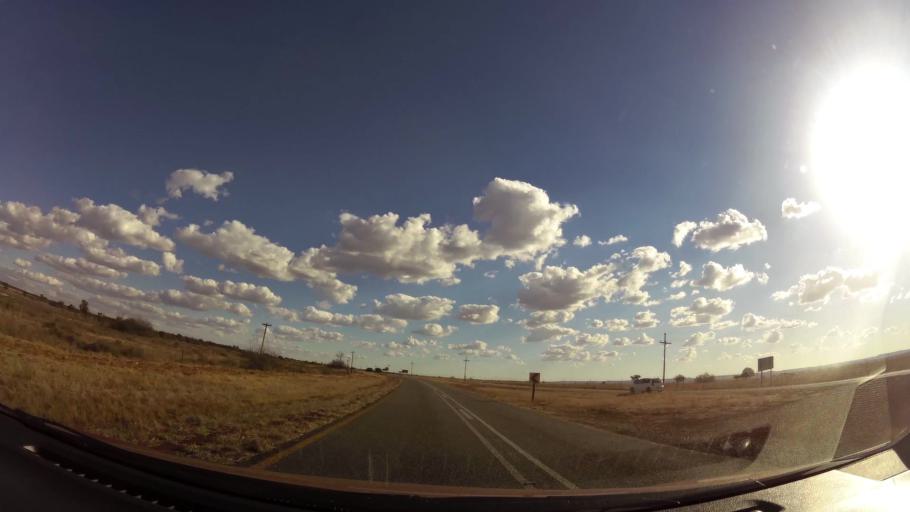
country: ZA
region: Gauteng
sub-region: West Rand District Municipality
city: Carletonville
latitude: -26.4131
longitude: 27.2359
